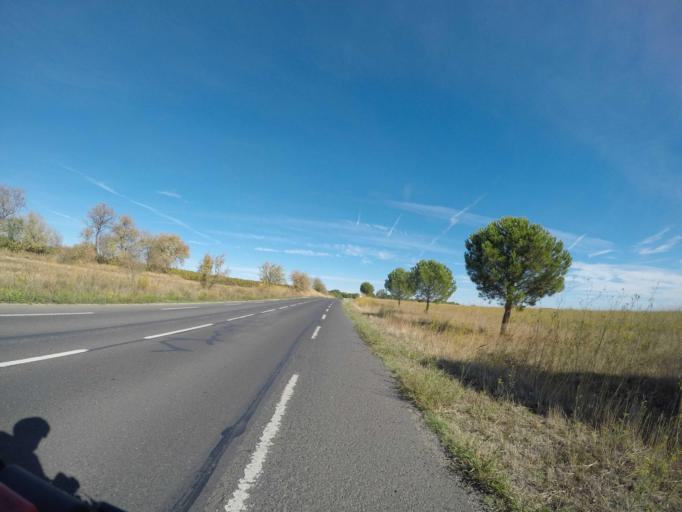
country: FR
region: Languedoc-Roussillon
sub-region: Departement des Pyrenees-Orientales
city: Ponteilla
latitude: 42.6196
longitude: 2.8111
